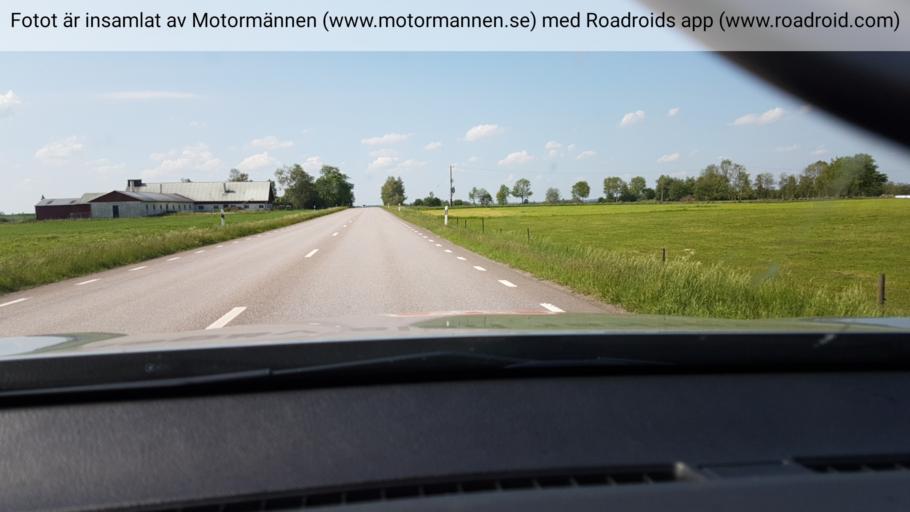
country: SE
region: Vaestra Goetaland
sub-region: Falkopings Kommun
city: Falkoeping
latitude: 58.1282
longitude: 13.5554
